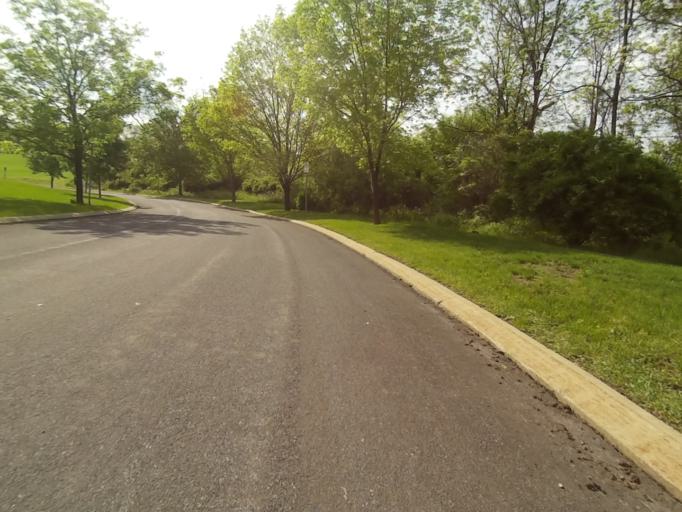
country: US
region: Pennsylvania
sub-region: Centre County
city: Houserville
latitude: 40.8250
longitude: -77.8242
